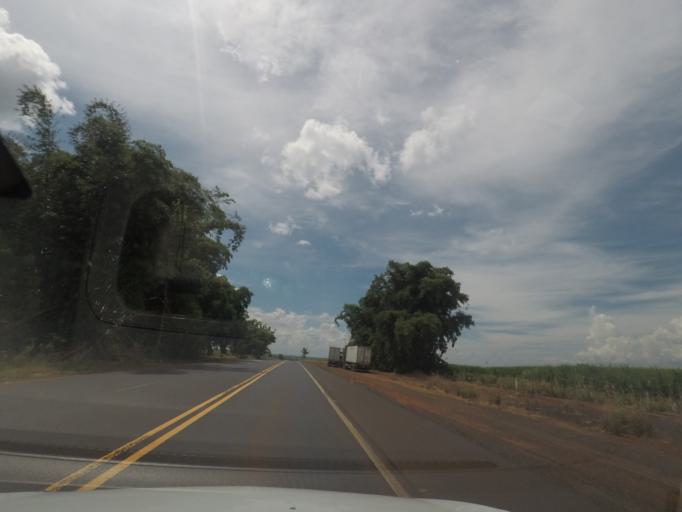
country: BR
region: Sao Paulo
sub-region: Barretos
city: Barretos
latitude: -20.2759
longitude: -48.6721
